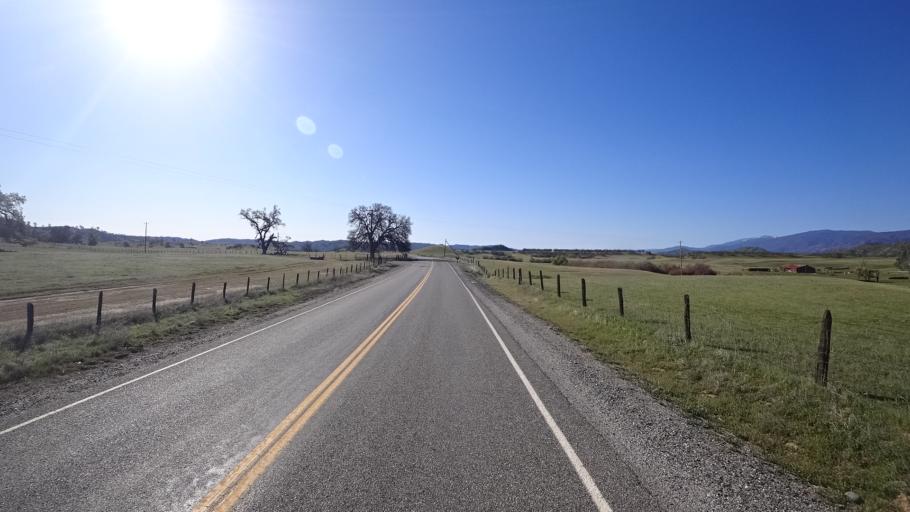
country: US
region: California
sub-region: Tehama County
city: Rancho Tehama Reserve
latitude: 39.6954
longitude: -122.5496
